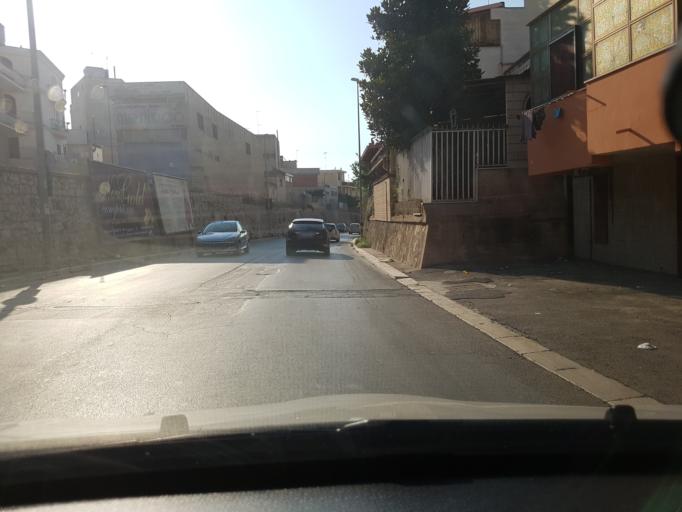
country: IT
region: Apulia
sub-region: Provincia di Foggia
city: Cerignola
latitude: 41.2687
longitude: 15.9015
